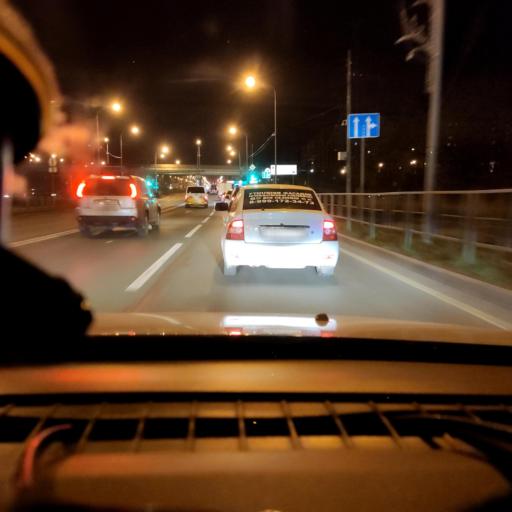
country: RU
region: Samara
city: Samara
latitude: 53.2704
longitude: 50.2230
